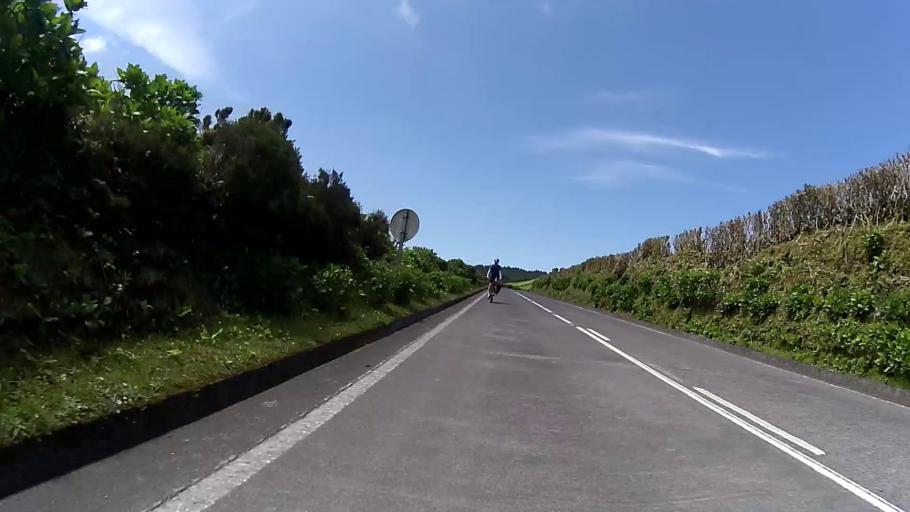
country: PT
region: Azores
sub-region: Ponta Delgada
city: Arrifes
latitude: 37.8422
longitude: -25.7742
